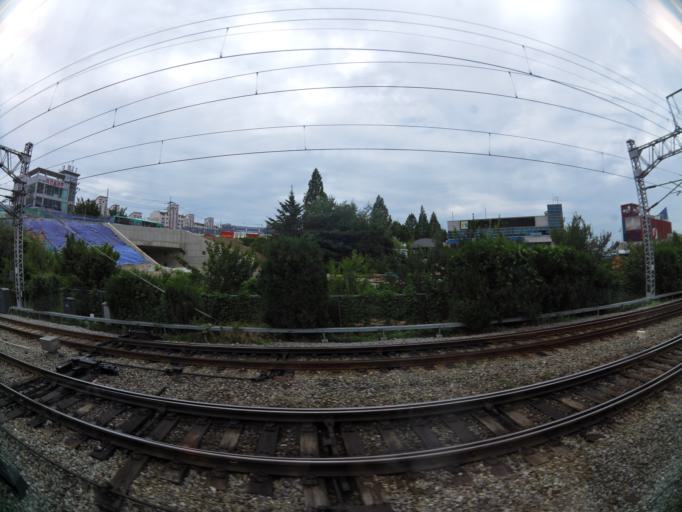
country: KR
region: Gyeonggi-do
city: Suwon-si
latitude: 37.2704
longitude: 126.9972
